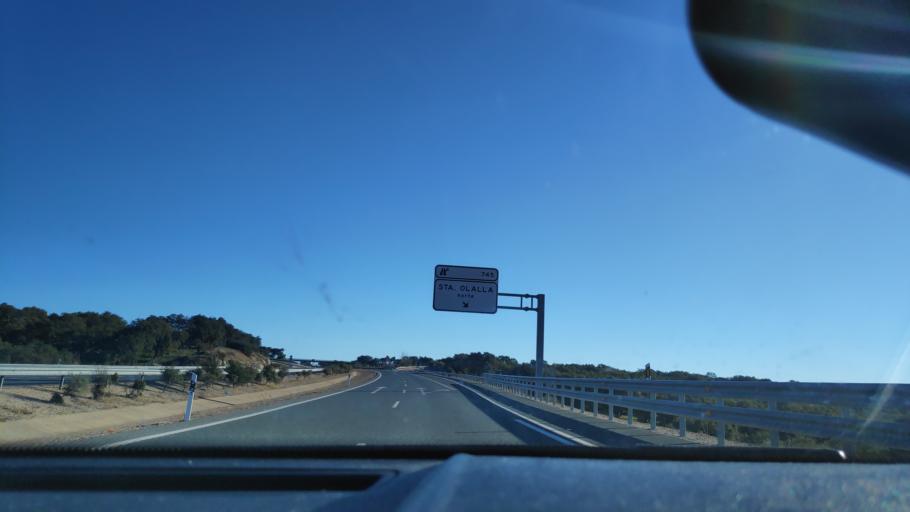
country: ES
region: Andalusia
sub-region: Provincia de Huelva
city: Santa Olalla del Cala
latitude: 37.9227
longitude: -6.2267
